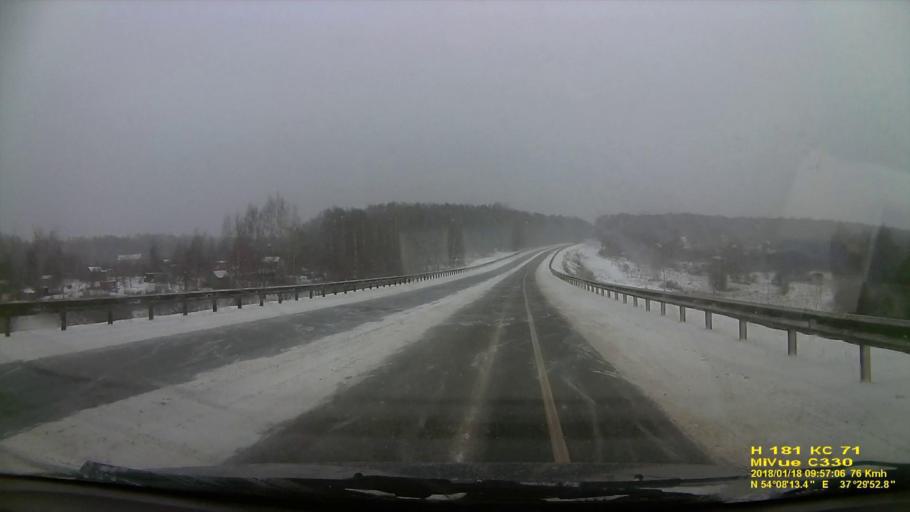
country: RU
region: Tula
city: Kosaya Gora
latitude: 54.1370
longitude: 37.4980
